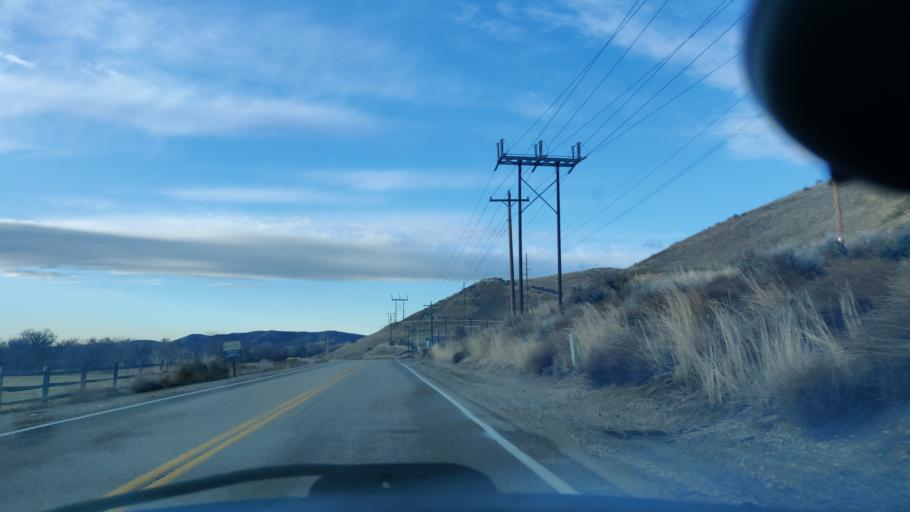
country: US
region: Idaho
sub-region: Ada County
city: Garden City
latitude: 43.7241
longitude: -116.2453
